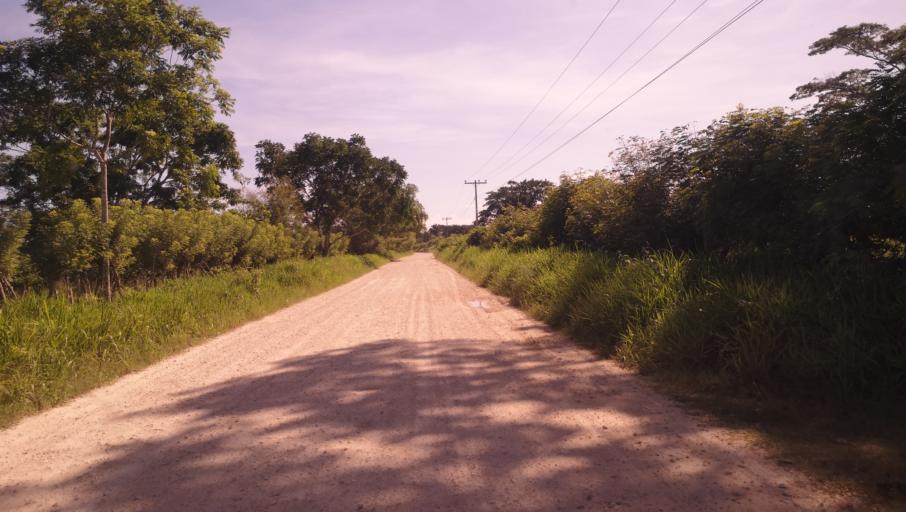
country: GT
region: Peten
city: Dolores
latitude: 16.7172
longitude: -89.3628
